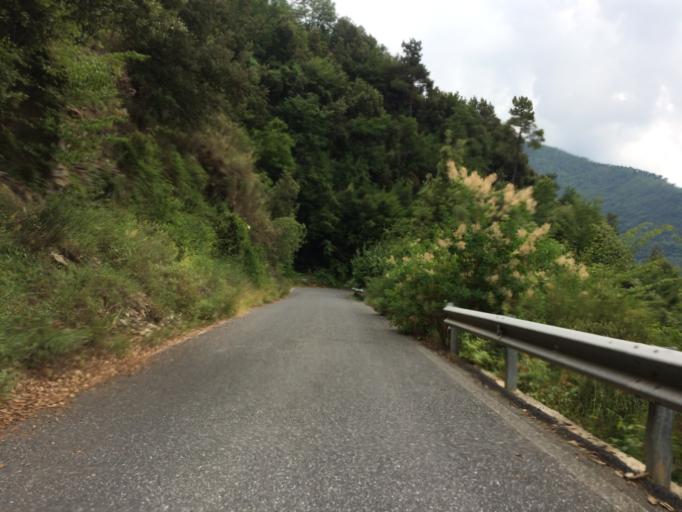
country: IT
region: Liguria
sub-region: Provincia di Imperia
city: Castel Vittorio
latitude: 43.9441
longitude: 7.6878
